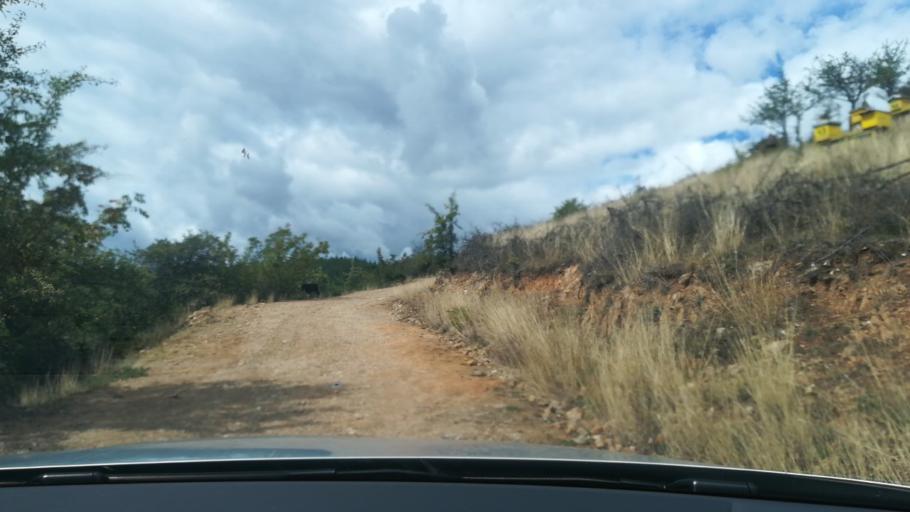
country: MK
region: Makedonska Kamenica
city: Makedonska Kamenica
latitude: 42.0035
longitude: 22.6100
